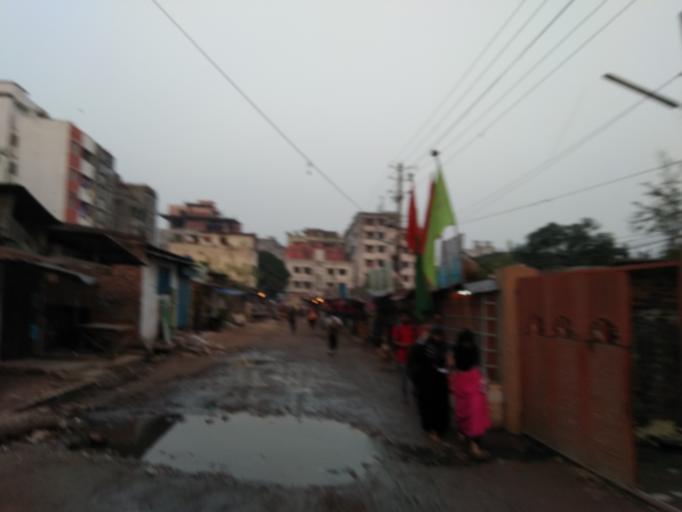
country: BD
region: Dhaka
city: Tungi
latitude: 23.8148
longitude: 90.3686
